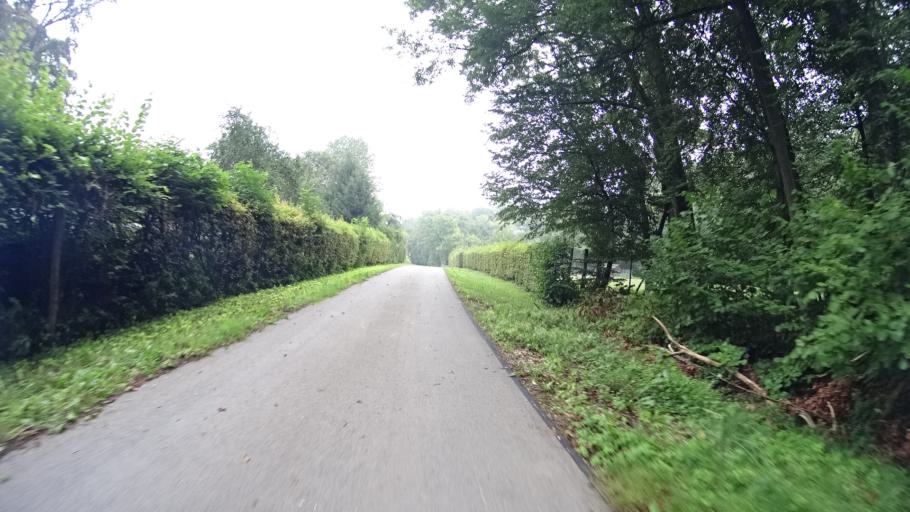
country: DE
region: Bavaria
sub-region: Upper Bavaria
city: Stammham
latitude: 48.8736
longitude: 11.5107
